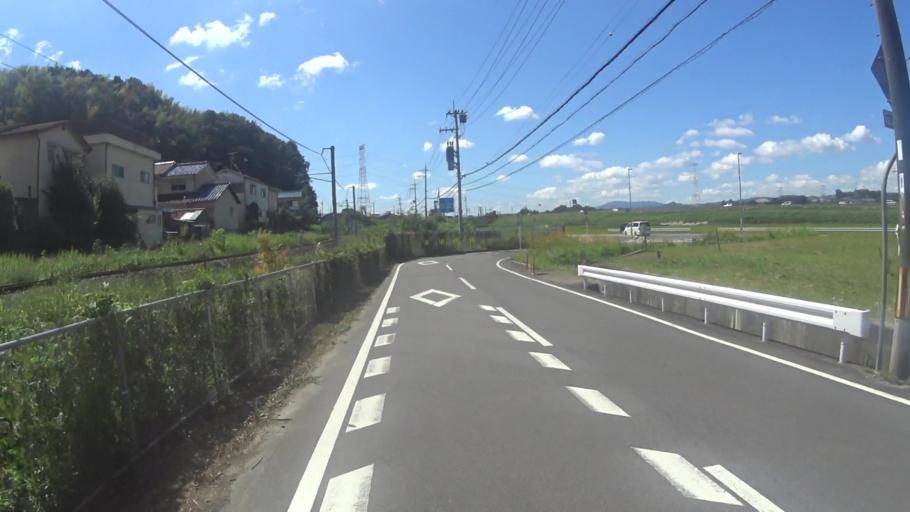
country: JP
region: Kyoto
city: Tanabe
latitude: 34.8105
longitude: 135.8072
